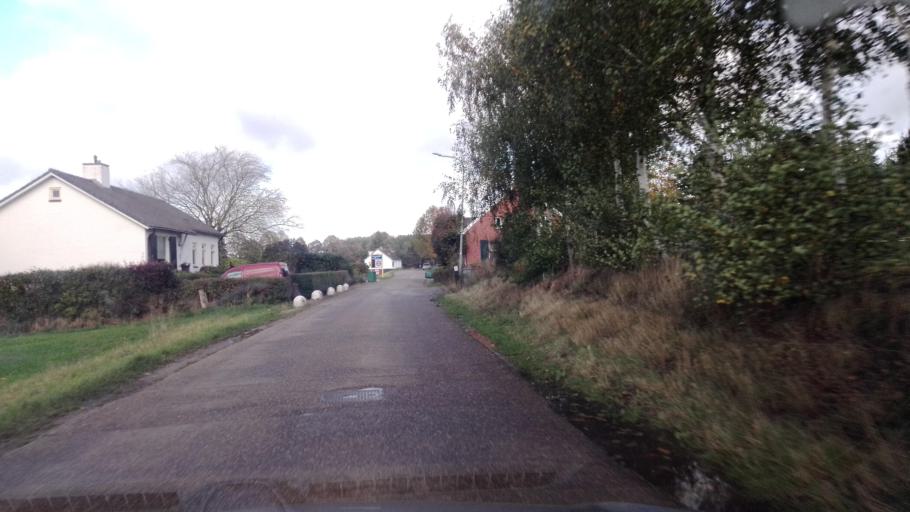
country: NL
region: Limburg
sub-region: Gemeente Venlo
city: Arcen
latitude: 51.4298
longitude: 6.1780
